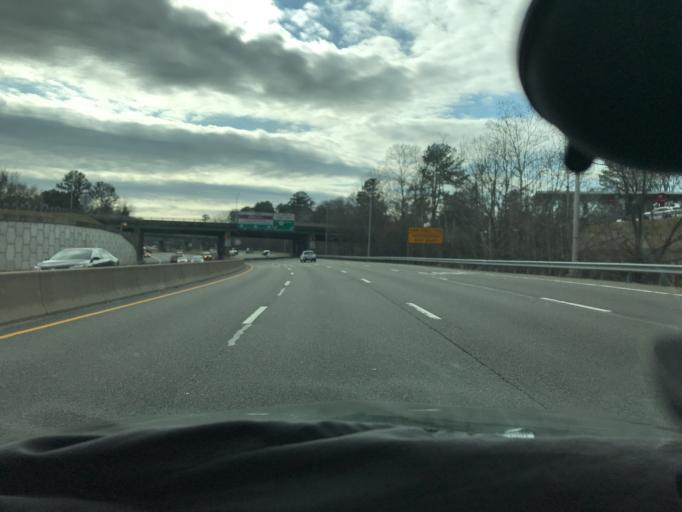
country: US
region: Virginia
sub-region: City of Richmond
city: Richmond
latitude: 37.5344
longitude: -77.5060
